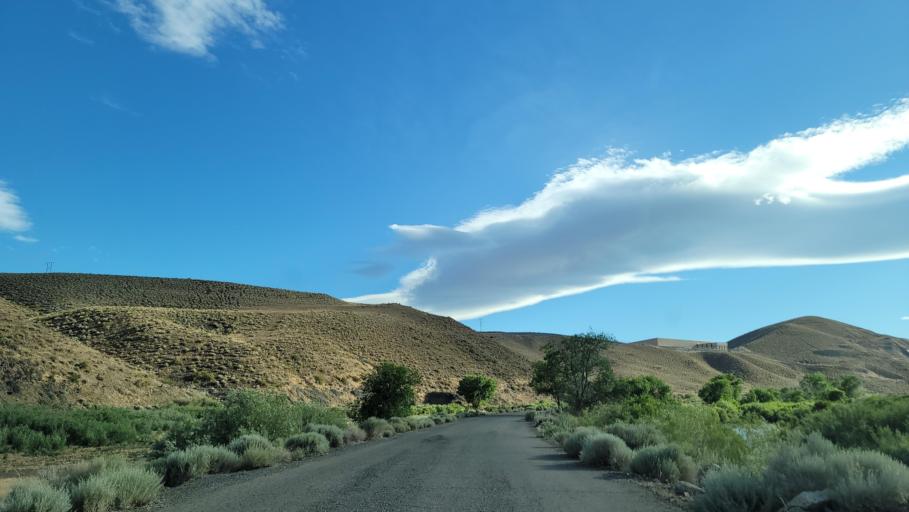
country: US
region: Nevada
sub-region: Washoe County
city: Sparks
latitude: 39.5120
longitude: -119.6208
